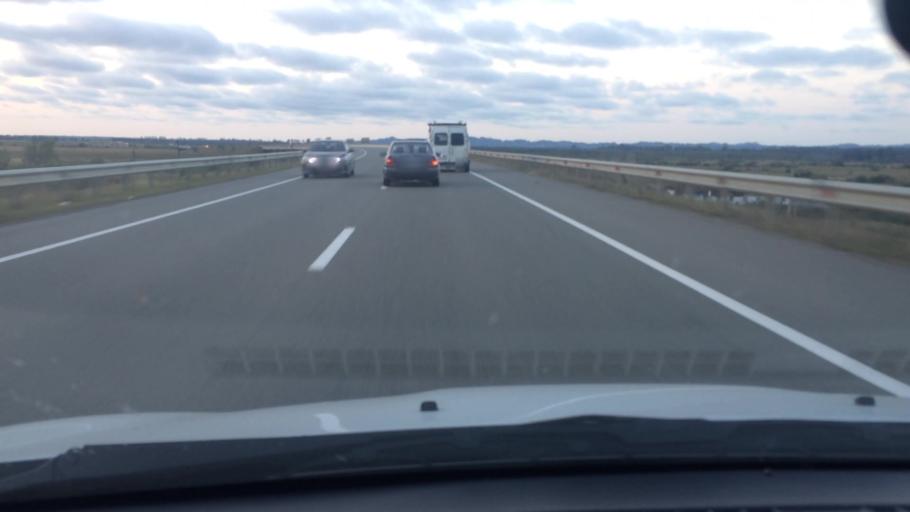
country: GE
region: Ajaria
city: Ochkhamuri
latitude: 41.8639
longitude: 41.8372
